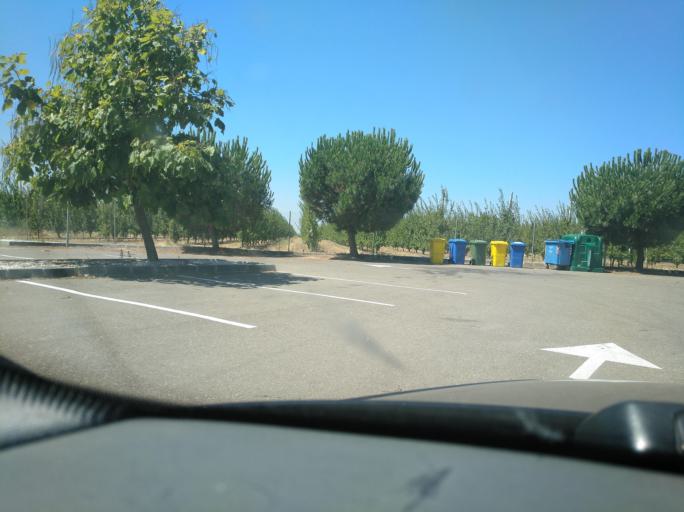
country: ES
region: Extremadura
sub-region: Provincia de Badajoz
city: Olivenza
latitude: 38.7351
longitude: -7.2300
